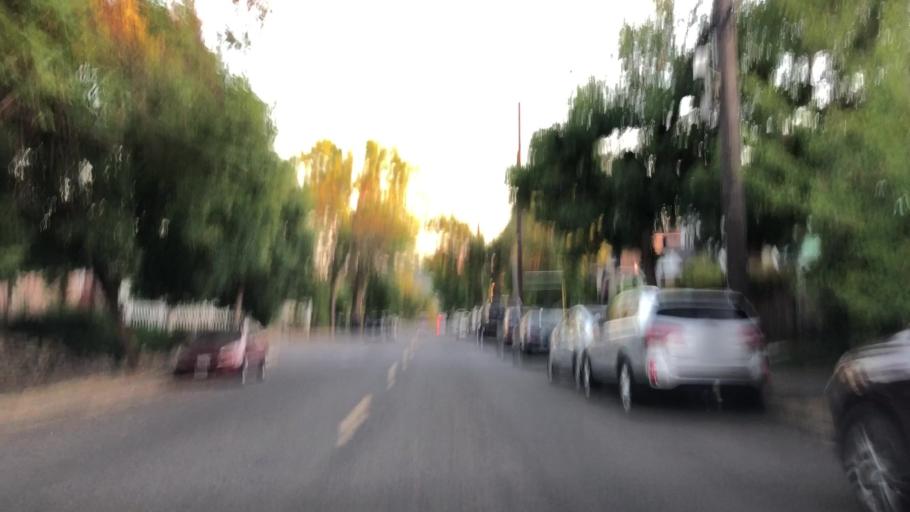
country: US
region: Washington
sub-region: King County
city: Seattle
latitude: 47.5957
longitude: -122.3062
